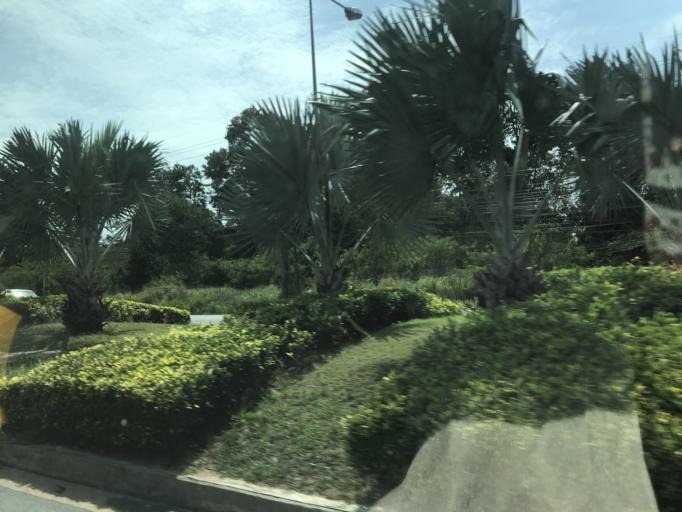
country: TH
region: Chon Buri
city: Bang Lamung
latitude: 13.0108
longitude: 100.9308
